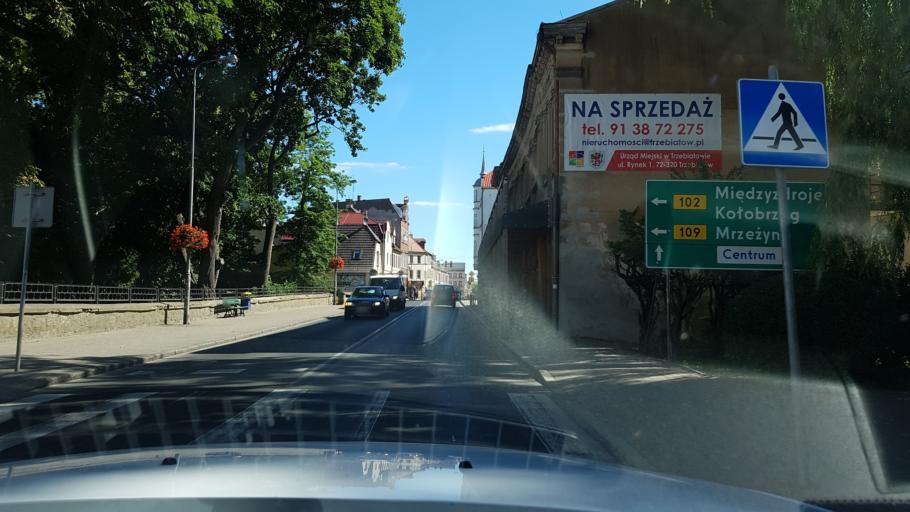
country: PL
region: West Pomeranian Voivodeship
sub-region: Powiat gryficki
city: Trzebiatow
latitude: 54.0605
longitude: 15.2635
